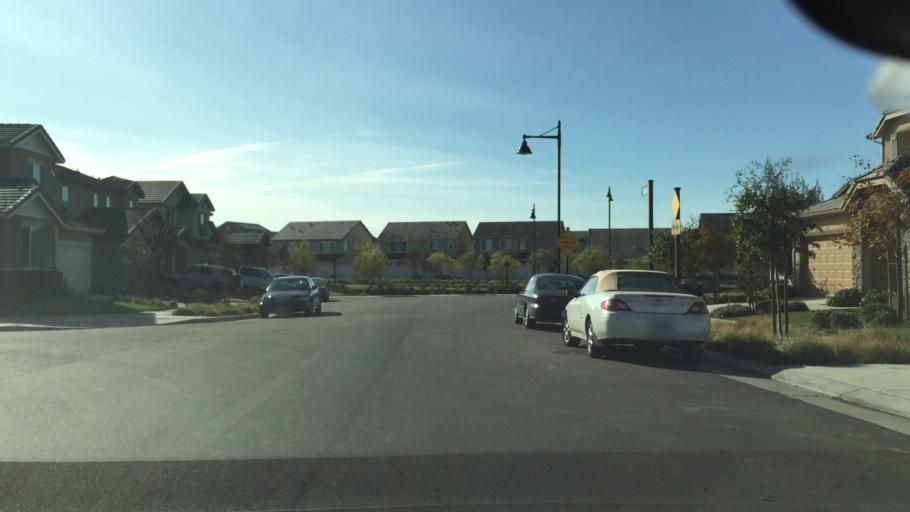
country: US
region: California
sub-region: San Joaquin County
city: Lathrop
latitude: 37.7939
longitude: -121.3200
